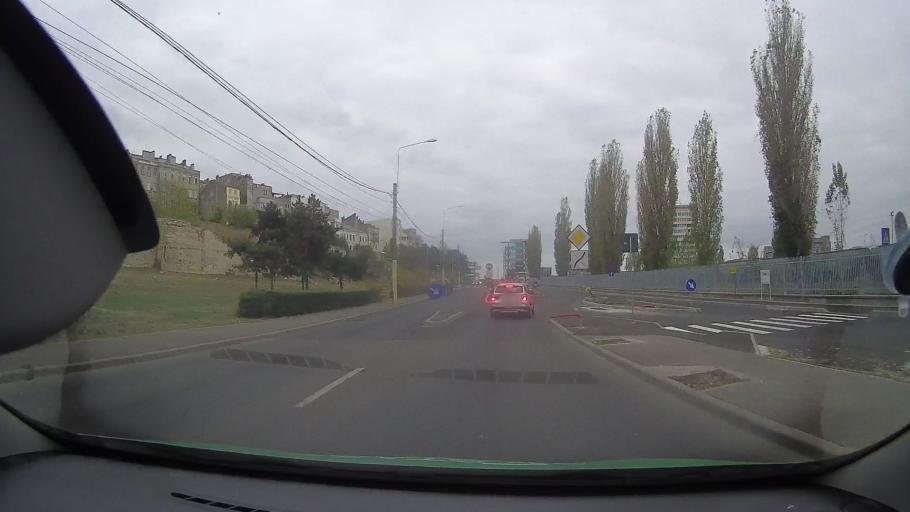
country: RO
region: Constanta
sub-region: Municipiul Constanta
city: Constanta
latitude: 44.1724
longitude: 28.6579
